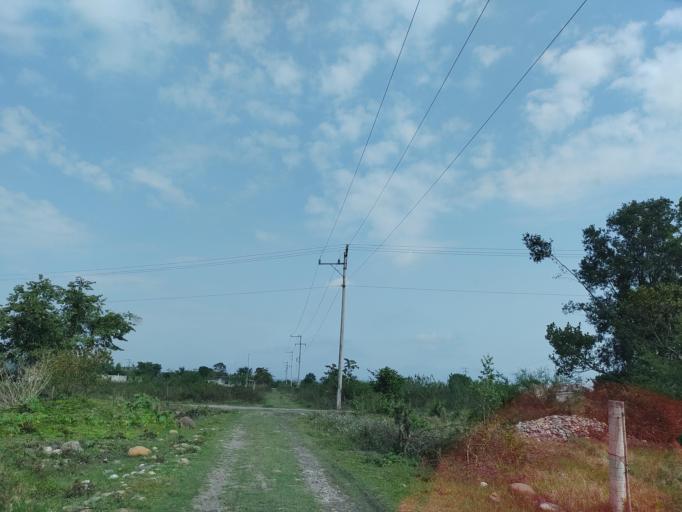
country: MX
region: Puebla
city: Espinal
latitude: 20.2792
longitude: -97.3334
